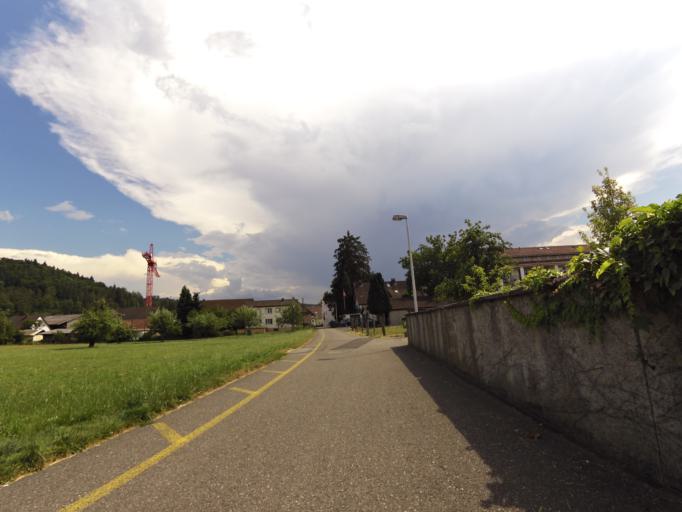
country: CH
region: Aargau
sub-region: Bezirk Brugg
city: Rupperswil
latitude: 47.3840
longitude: 8.1213
